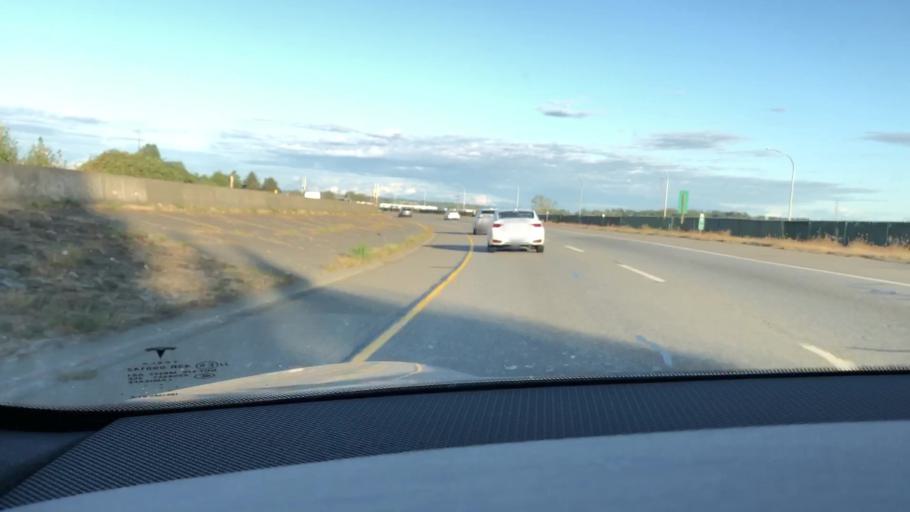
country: CA
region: British Columbia
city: New Westminster
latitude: 49.1700
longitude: -123.0046
